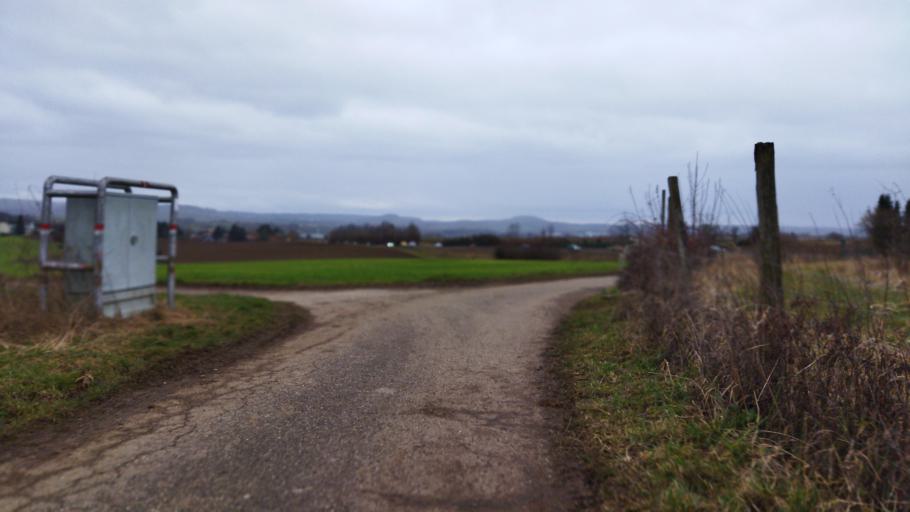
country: DE
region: Baden-Wuerttemberg
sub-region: Regierungsbezirk Stuttgart
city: Untergruppenbach
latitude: 49.0979
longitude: 9.2641
